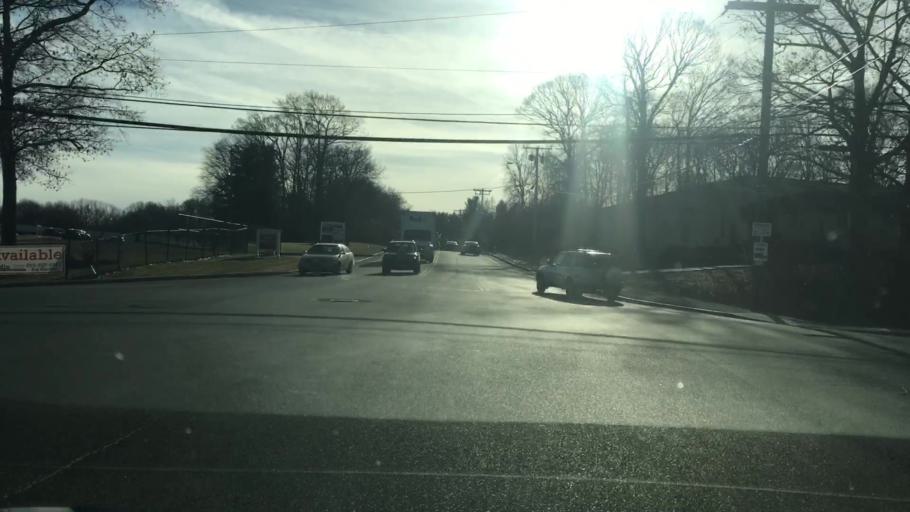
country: US
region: Connecticut
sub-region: New Haven County
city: Prospect
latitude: 41.5392
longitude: -72.9760
